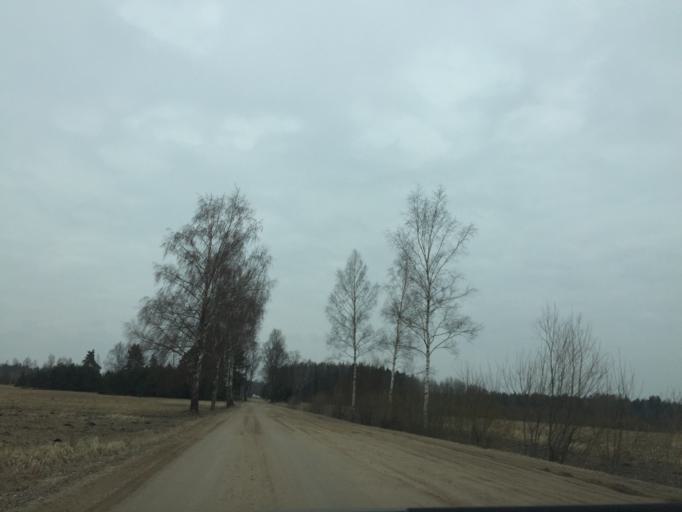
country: LV
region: Kekava
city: Kekava
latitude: 56.8013
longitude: 24.1649
